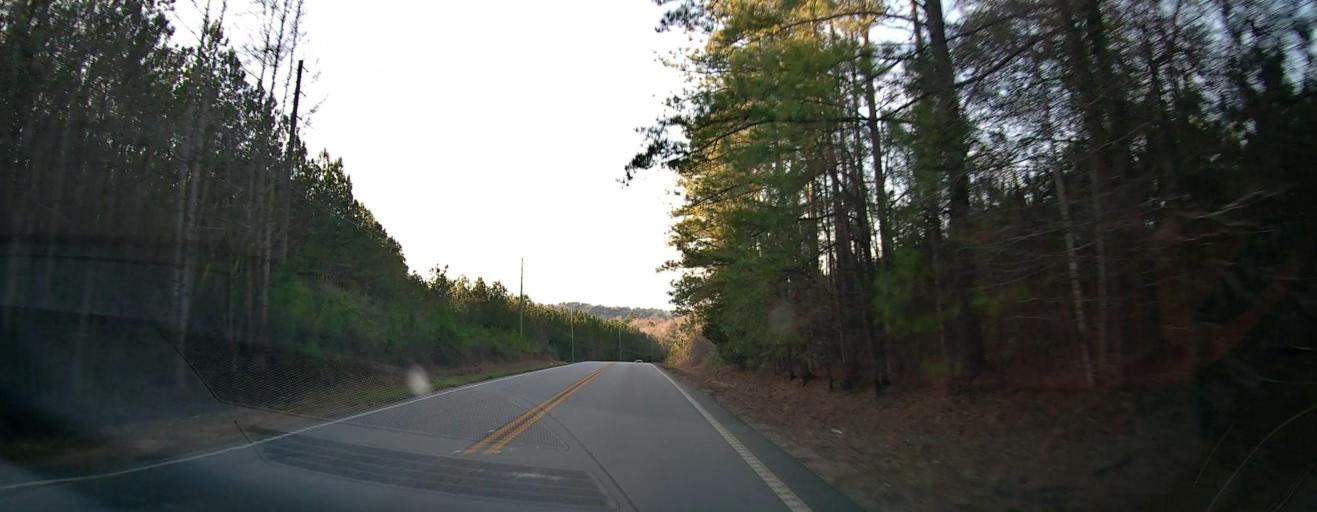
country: US
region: Alabama
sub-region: Chambers County
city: Valley
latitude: 32.8428
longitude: -85.1226
